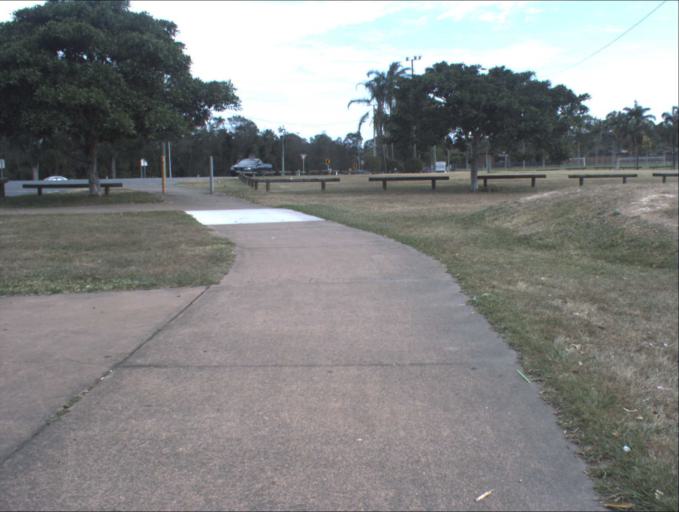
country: AU
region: Queensland
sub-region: Logan
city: Beenleigh
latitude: -27.7073
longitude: 153.1951
